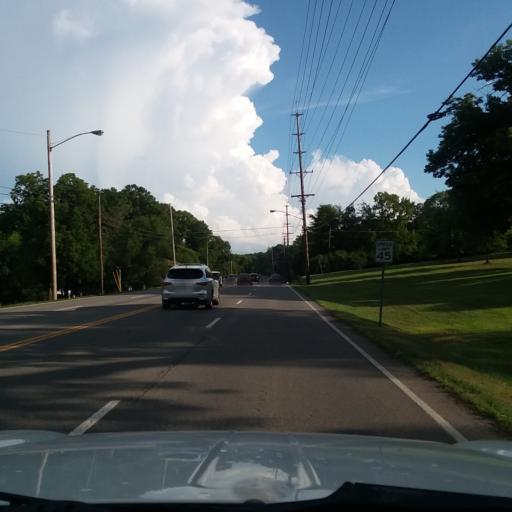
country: US
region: Tennessee
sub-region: Davidson County
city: Oak Hill
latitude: 36.0761
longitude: -86.7734
